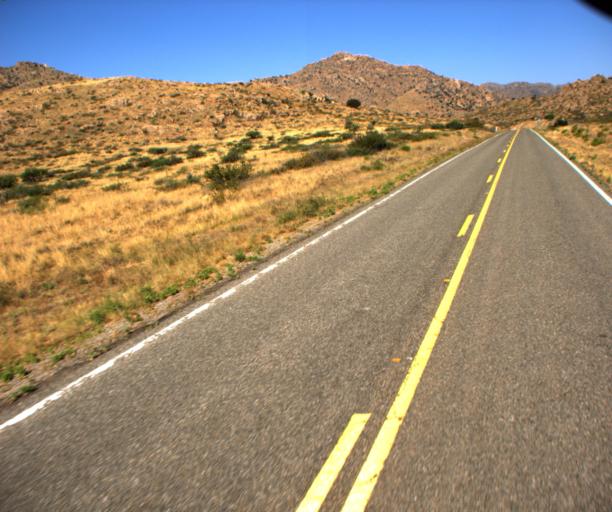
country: US
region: Arizona
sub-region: Graham County
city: Swift Trail Junction
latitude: 32.5610
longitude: -109.7761
